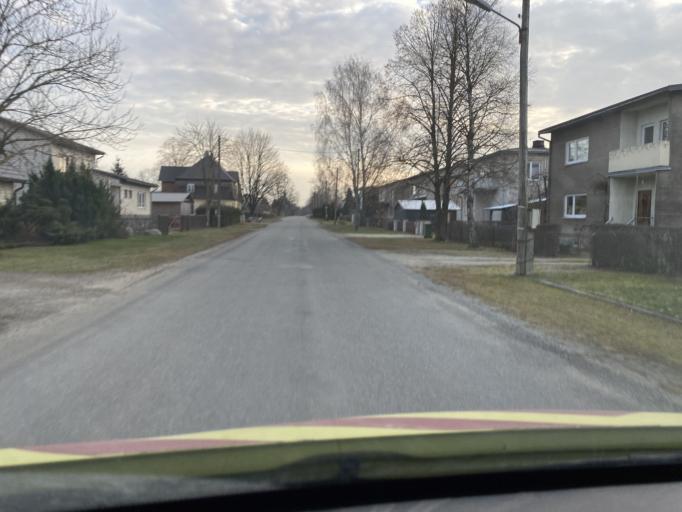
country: EE
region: Jogevamaa
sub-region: Poltsamaa linn
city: Poltsamaa
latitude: 58.6494
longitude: 25.9658
